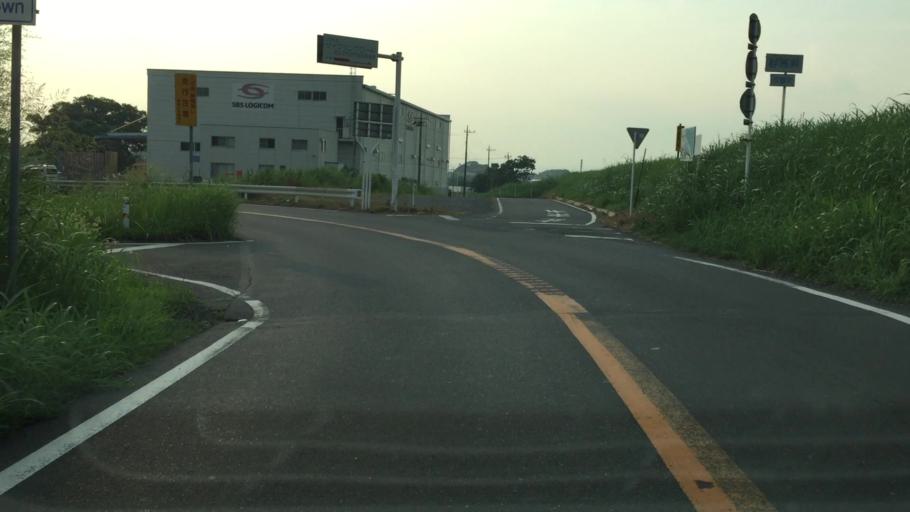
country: JP
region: Tochigi
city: Fujioka
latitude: 36.2617
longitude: 139.6366
